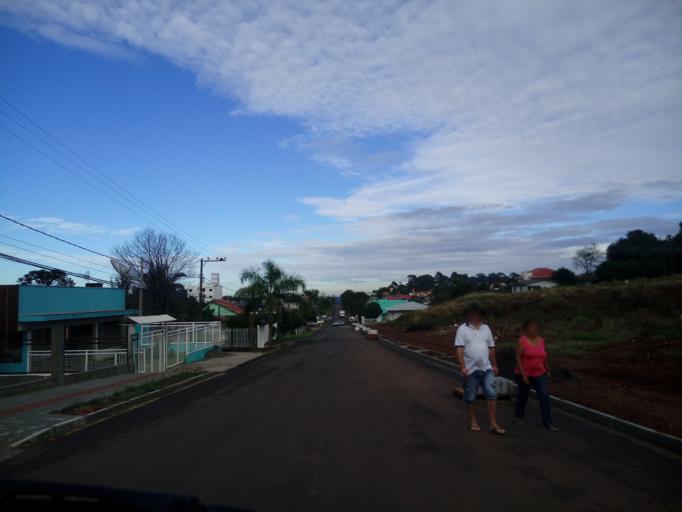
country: BR
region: Santa Catarina
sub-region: Chapeco
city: Chapeco
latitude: -27.1081
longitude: -52.6295
